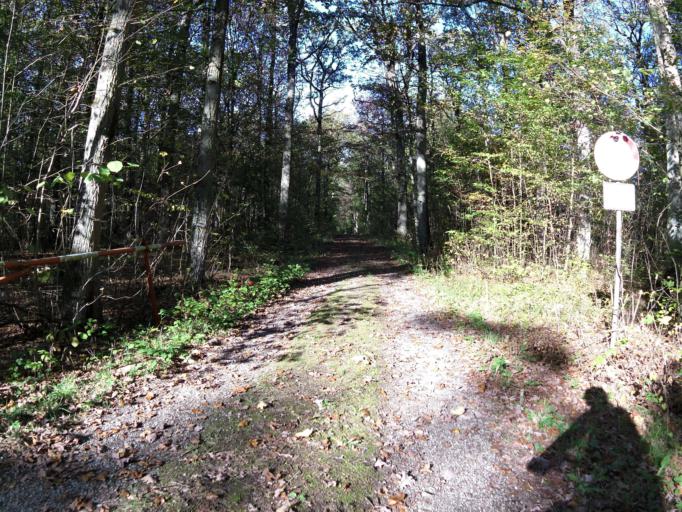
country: DE
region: Bavaria
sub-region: Regierungsbezirk Unterfranken
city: Sulzfeld am Main
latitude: 49.7186
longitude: 10.0898
